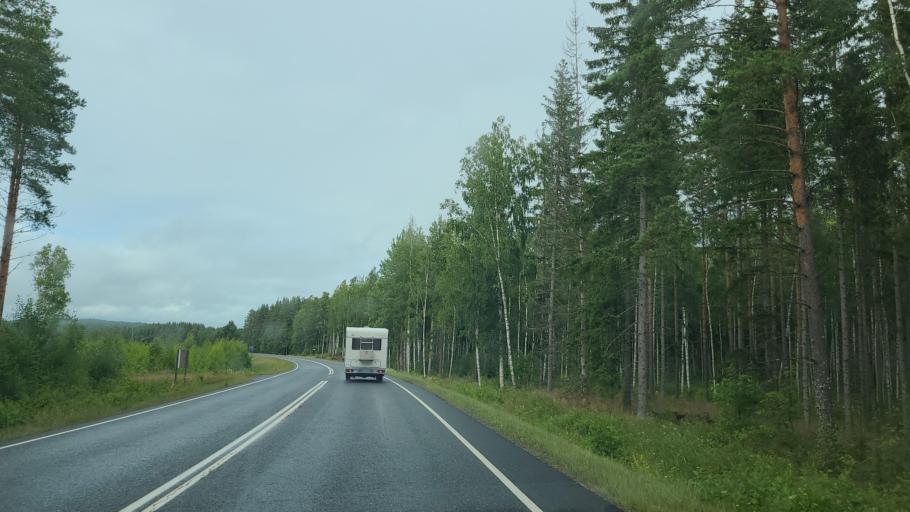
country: FI
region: Varsinais-Suomi
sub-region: Turku
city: Sauvo
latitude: 60.3248
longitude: 22.7133
